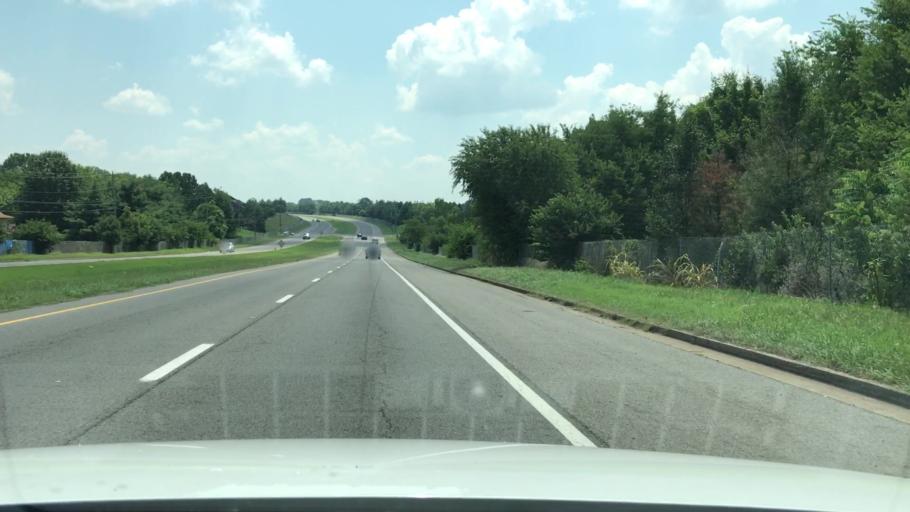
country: US
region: Tennessee
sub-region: Sumner County
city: Gallatin
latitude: 36.3708
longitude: -86.4620
